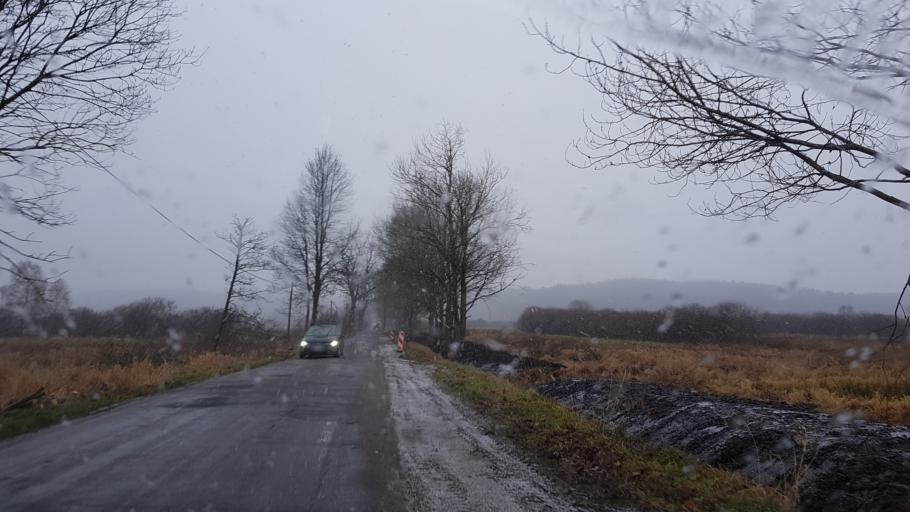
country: PL
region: West Pomeranian Voivodeship
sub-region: Powiat slawienski
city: Slawno
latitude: 54.2625
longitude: 16.5861
